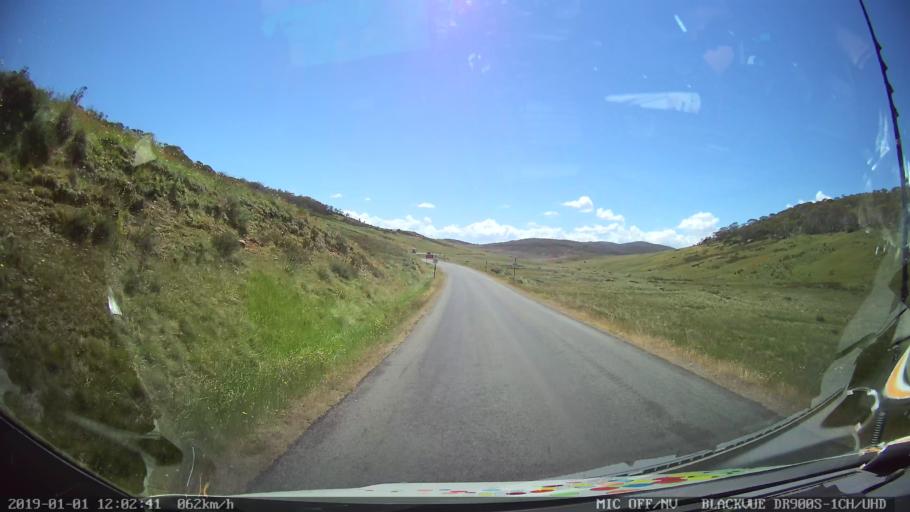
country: AU
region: New South Wales
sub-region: Snowy River
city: Jindabyne
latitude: -35.8713
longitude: 148.4794
